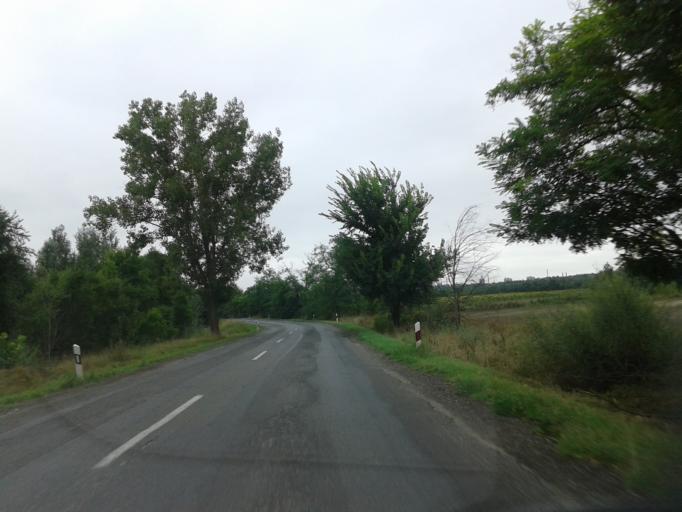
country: HU
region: Bacs-Kiskun
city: Szalkszentmarton
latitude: 46.9643
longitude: 18.9829
